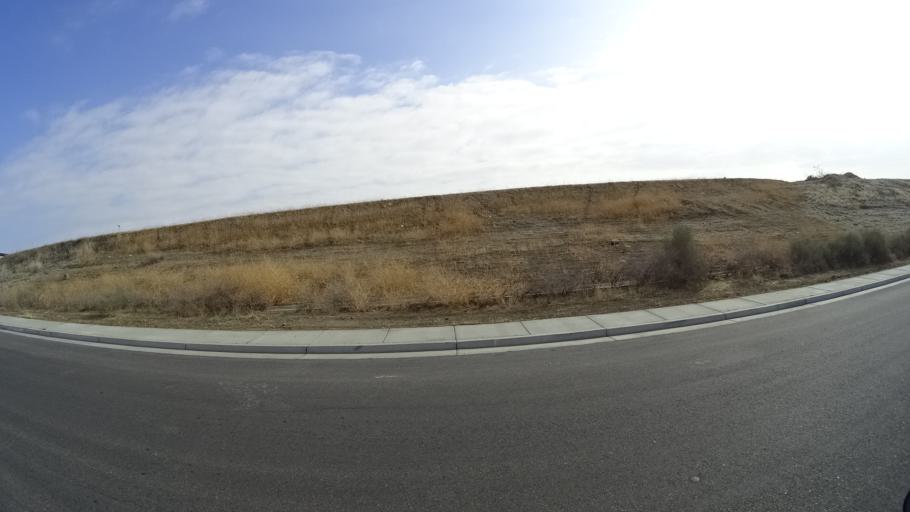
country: US
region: California
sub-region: Kern County
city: Bakersfield
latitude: 35.3936
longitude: -118.9194
